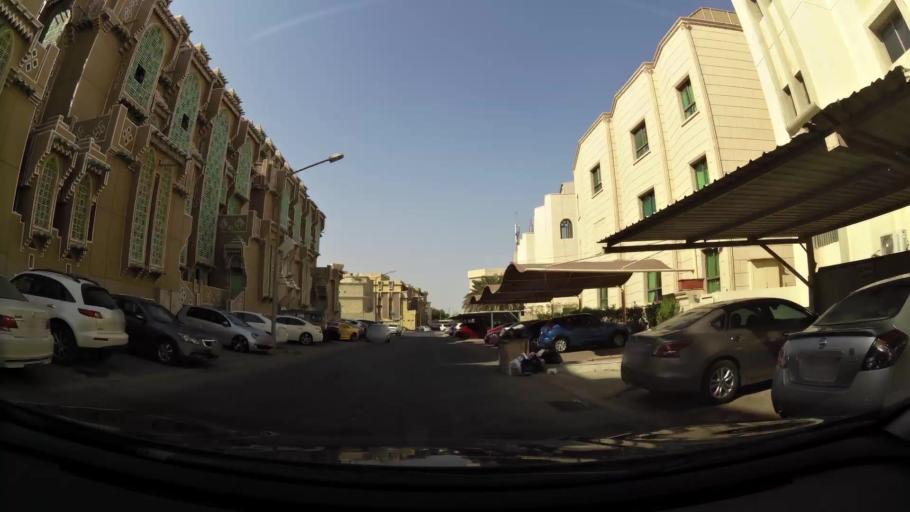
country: KW
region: Muhafazat Hawalli
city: Salwa
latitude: 29.2872
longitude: 48.0752
